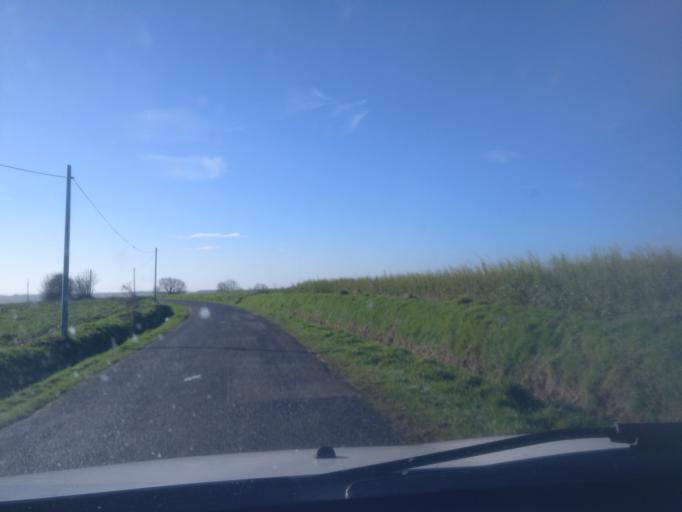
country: FR
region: Brittany
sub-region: Departement d'Ille-et-Vilaine
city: Roz-sur-Couesnon
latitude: 48.5472
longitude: -1.6227
